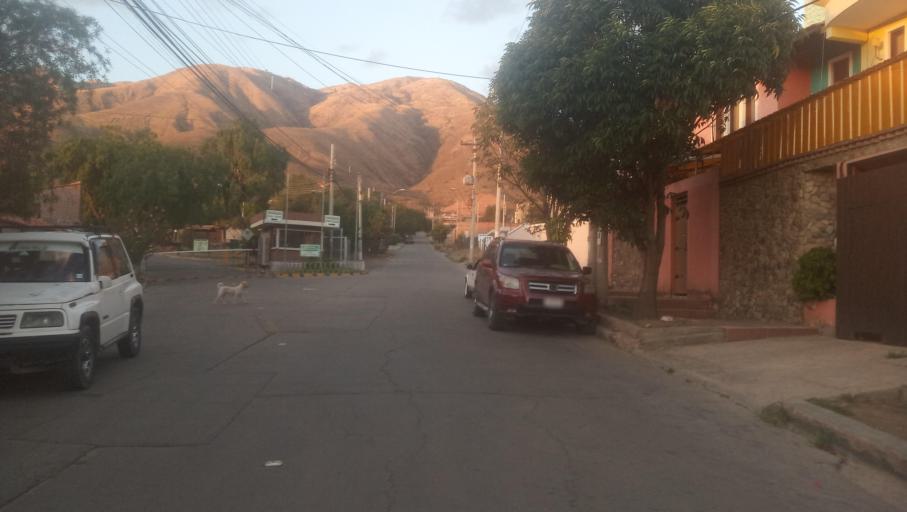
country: BO
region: Cochabamba
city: Cochabamba
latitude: -17.3748
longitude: -66.0953
